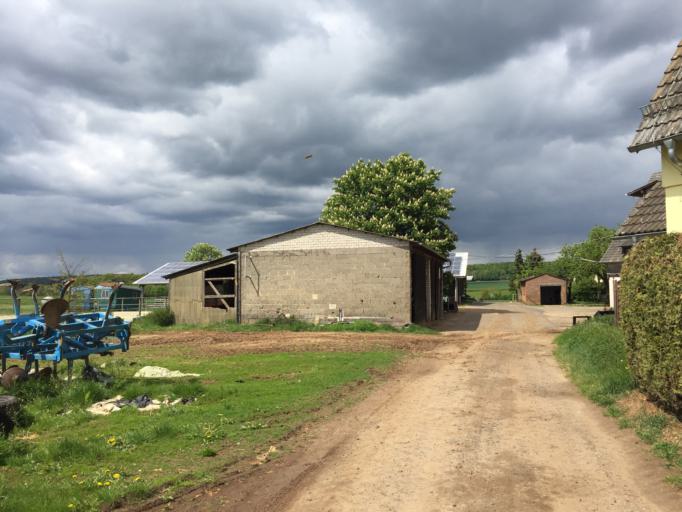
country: DE
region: Hesse
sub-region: Regierungsbezirk Giessen
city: Reiskirchen
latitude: 50.5720
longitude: 8.8720
